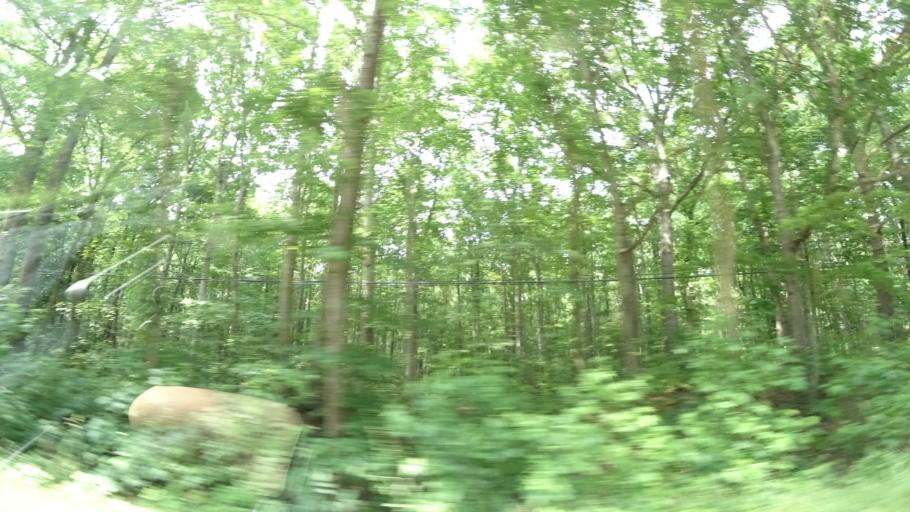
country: US
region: Virginia
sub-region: Spotsylvania County
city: Spotsylvania Courthouse
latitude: 38.1428
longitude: -77.5755
